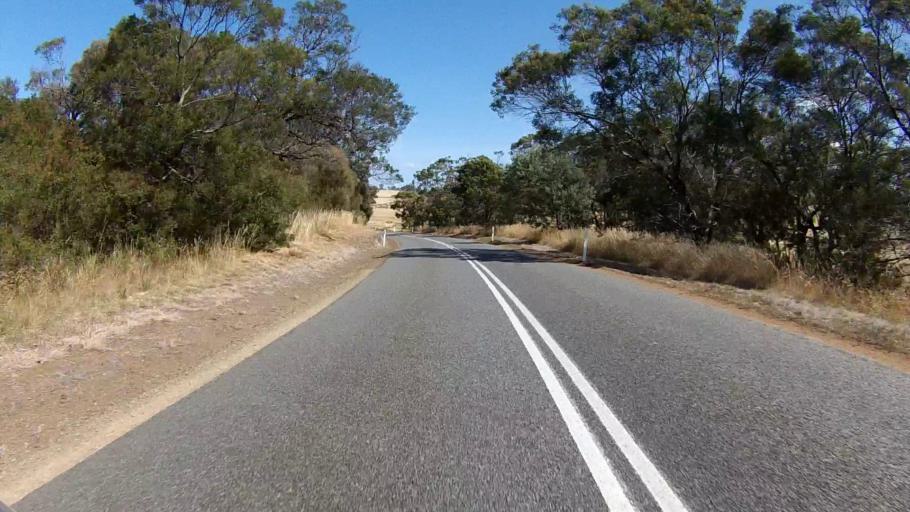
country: AU
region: Tasmania
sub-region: Sorell
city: Sorell
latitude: -42.2919
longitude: 147.9905
